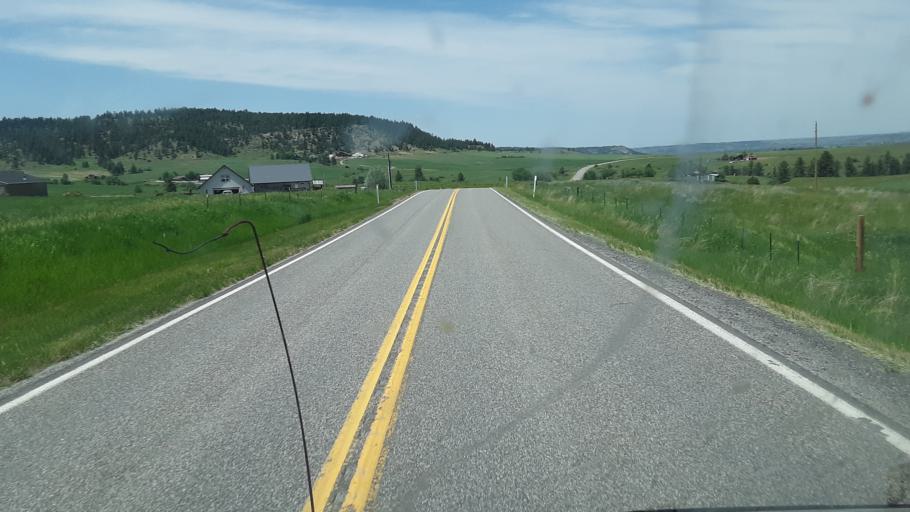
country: US
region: Montana
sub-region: Stillwater County
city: Columbus
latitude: 45.5793
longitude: -109.1793
